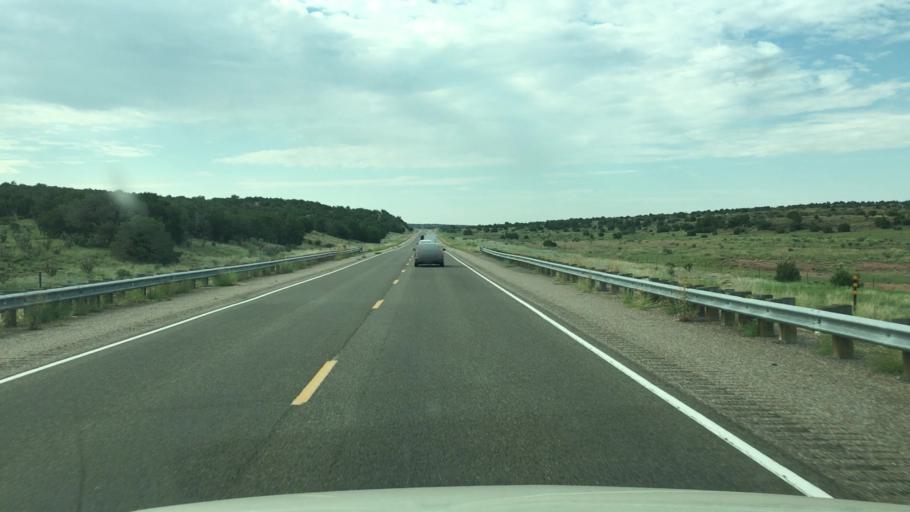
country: US
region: New Mexico
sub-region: Santa Fe County
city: Eldorado at Santa Fe
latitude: 35.3029
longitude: -105.8278
